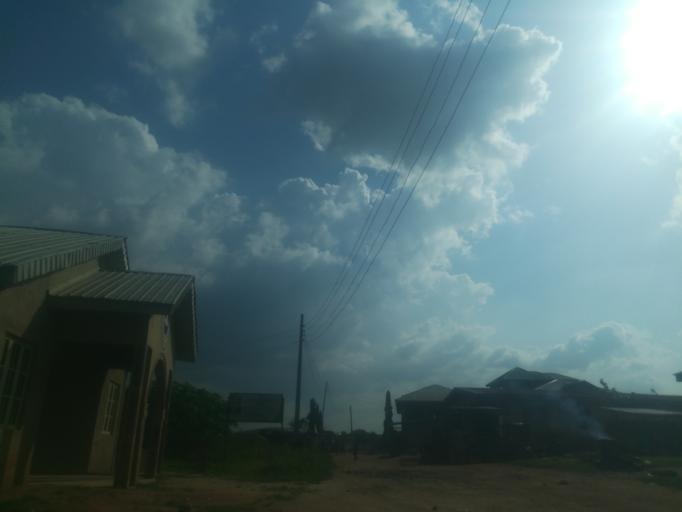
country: NG
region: Oyo
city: Moniya
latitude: 7.5122
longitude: 3.9109
